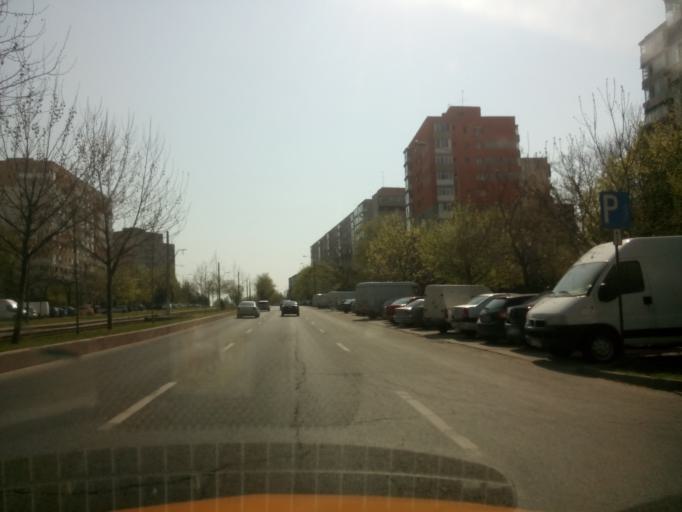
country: RO
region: Ilfov
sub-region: Comuna Popesti-Leordeni
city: Popesti-Leordeni
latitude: 44.4117
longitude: 26.1686
